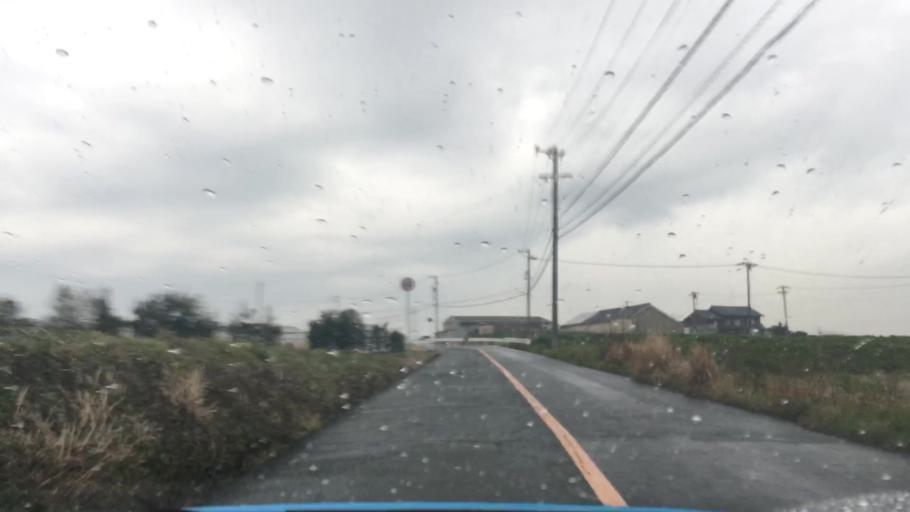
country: JP
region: Aichi
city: Toyohashi
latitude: 34.6814
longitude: 137.3900
